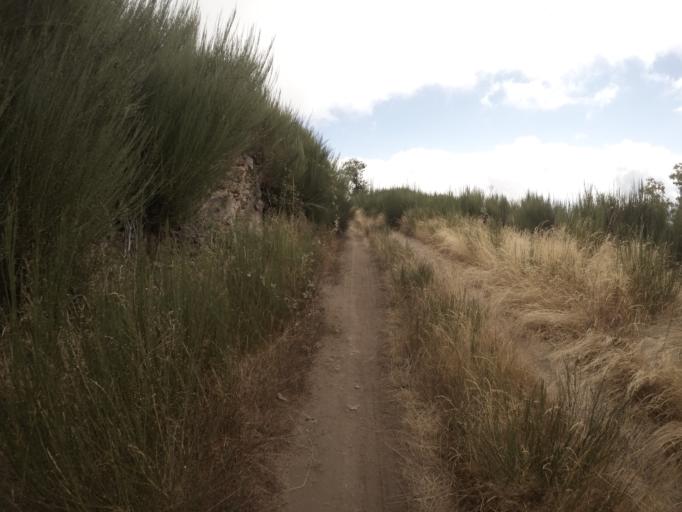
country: PT
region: Madeira
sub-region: Camara de Lobos
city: Curral das Freiras
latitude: 32.7126
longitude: -16.9934
